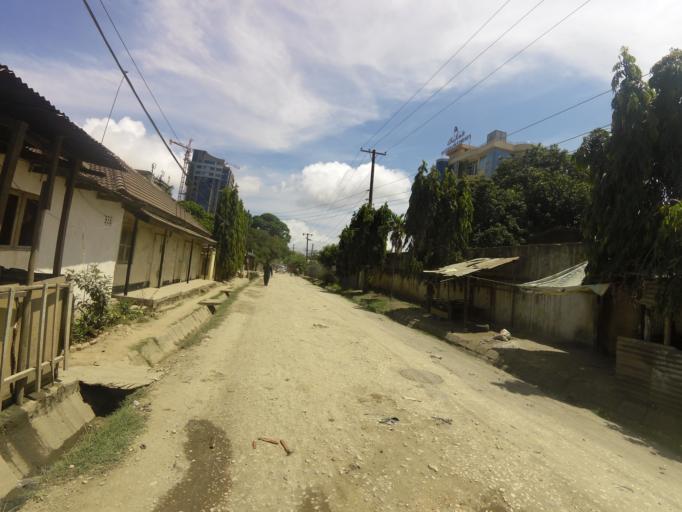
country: TZ
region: Dar es Salaam
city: Magomeni
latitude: -6.7766
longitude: 39.2438
